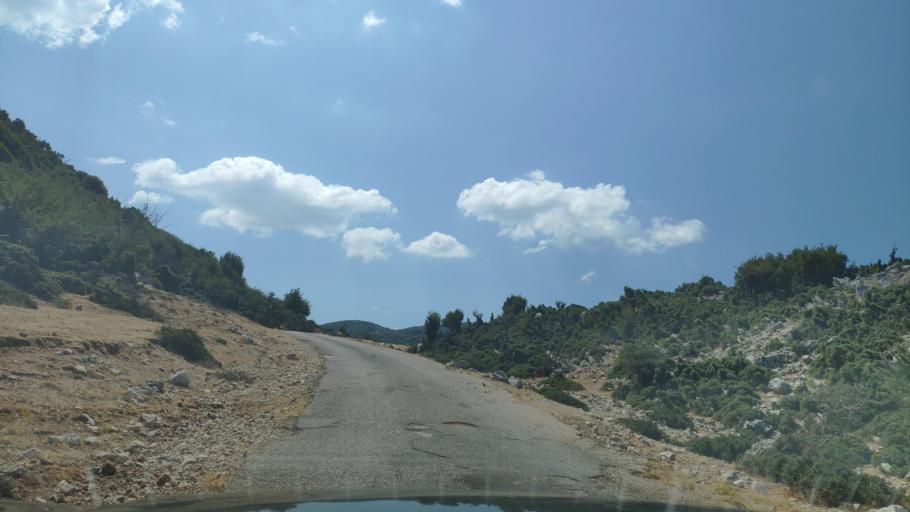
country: GR
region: West Greece
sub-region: Nomos Aitolias kai Akarnanias
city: Monastirakion
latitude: 38.8025
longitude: 20.9474
